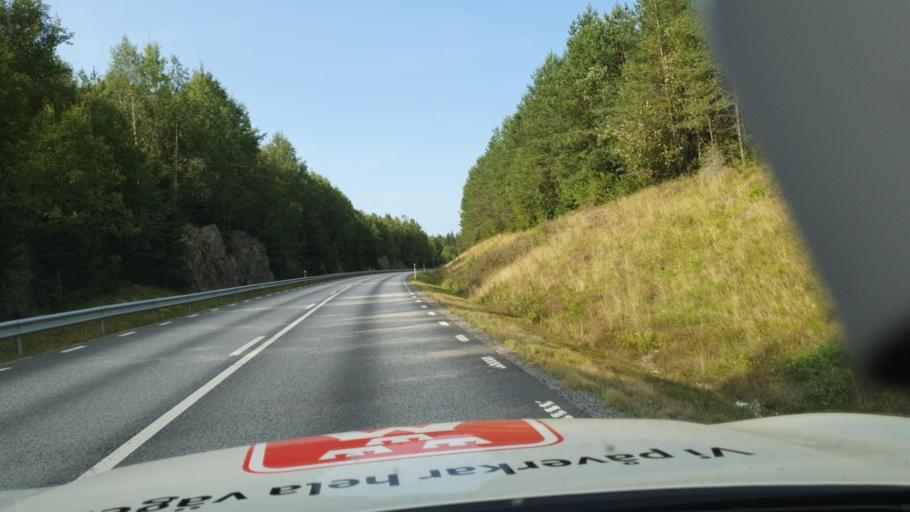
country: SE
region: Vaestra Goetaland
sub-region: Dals-Ed Kommun
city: Ed
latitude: 58.8504
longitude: 11.7069
